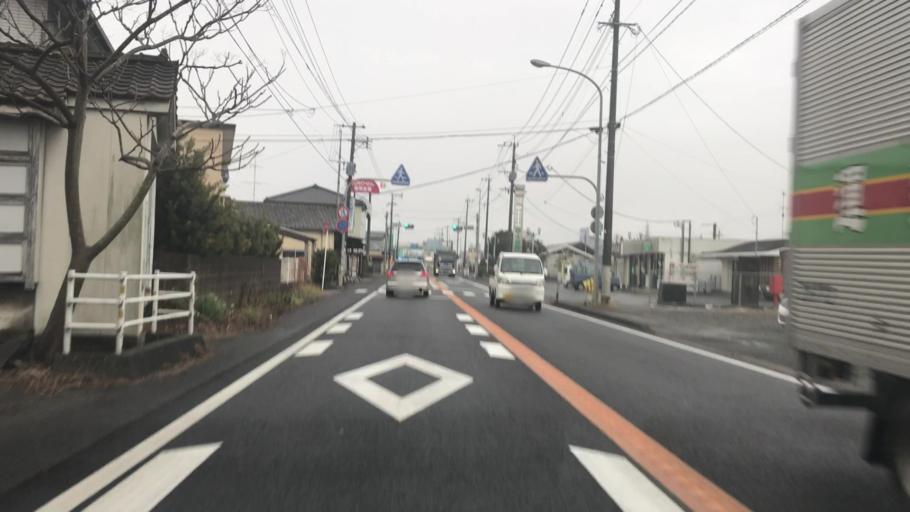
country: JP
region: Saga Prefecture
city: Takeocho-takeo
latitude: 33.2129
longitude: 130.1051
